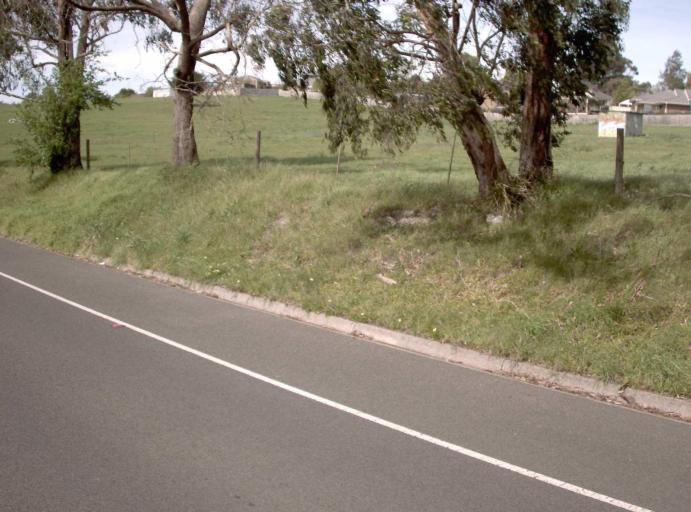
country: AU
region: Victoria
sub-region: Yarra Ranges
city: Kilsyth
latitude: -37.7819
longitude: 145.3250
